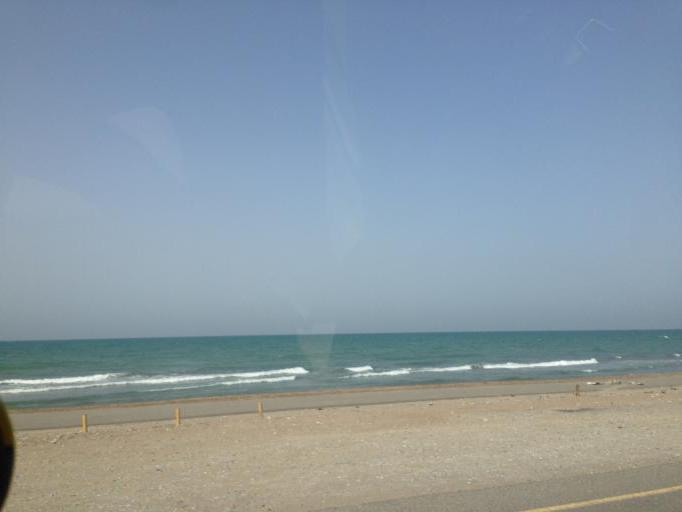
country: OM
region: Al Batinah
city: Barka'
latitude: 23.7251
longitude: 57.8465
